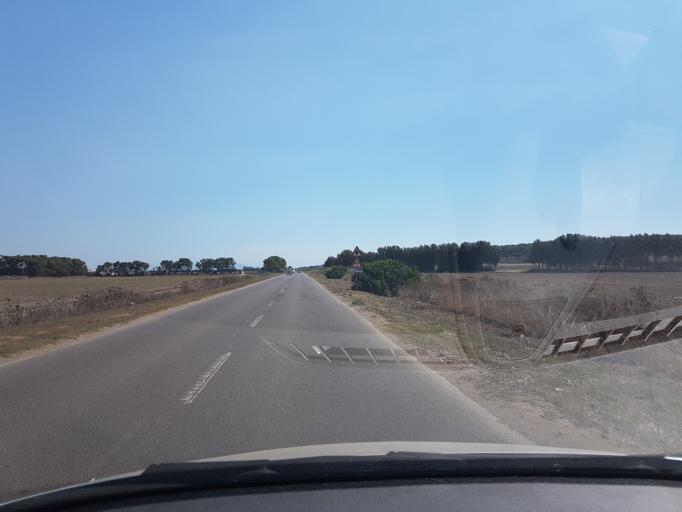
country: IT
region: Sardinia
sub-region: Provincia di Oristano
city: Nurachi
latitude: 39.9709
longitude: 8.4527
